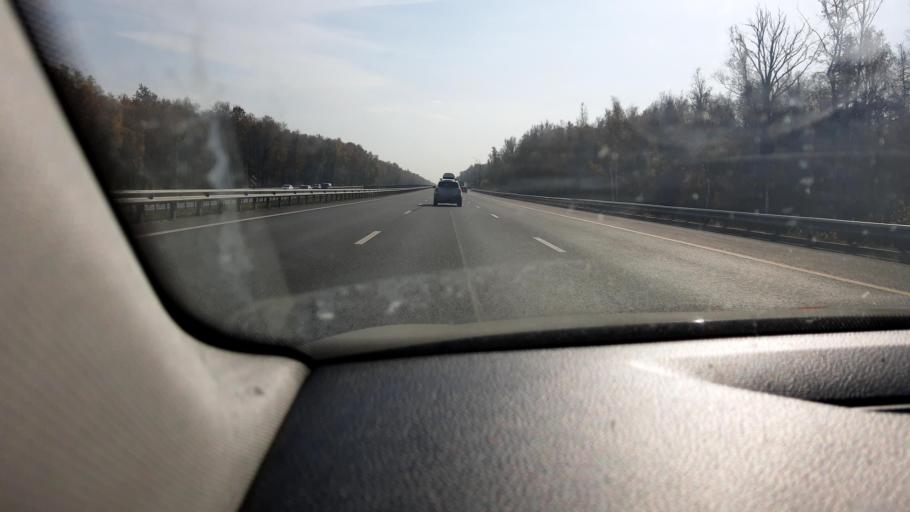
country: RU
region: Moskovskaya
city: Stupino
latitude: 54.9199
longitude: 38.0012
